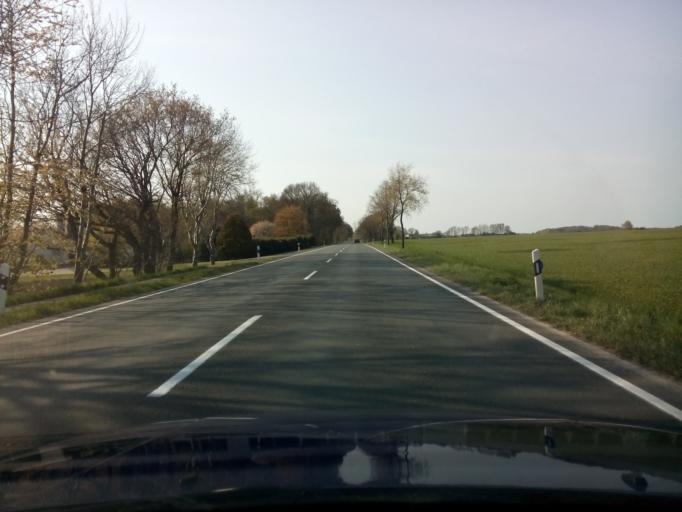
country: DE
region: Lower Saxony
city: Sustedt
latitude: 52.8504
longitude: 8.8938
